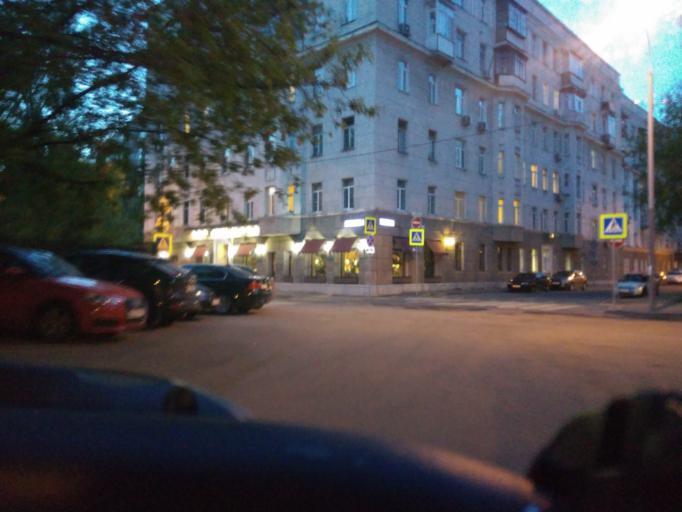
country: RU
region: Moscow
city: Taganskiy
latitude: 55.7410
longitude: 37.6651
